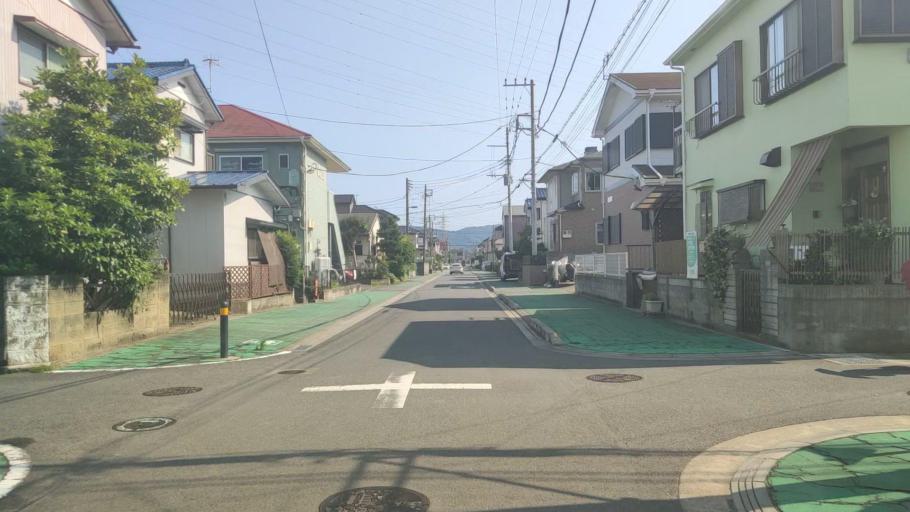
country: JP
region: Kanagawa
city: Hiratsuka
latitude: 35.3494
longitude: 139.3227
